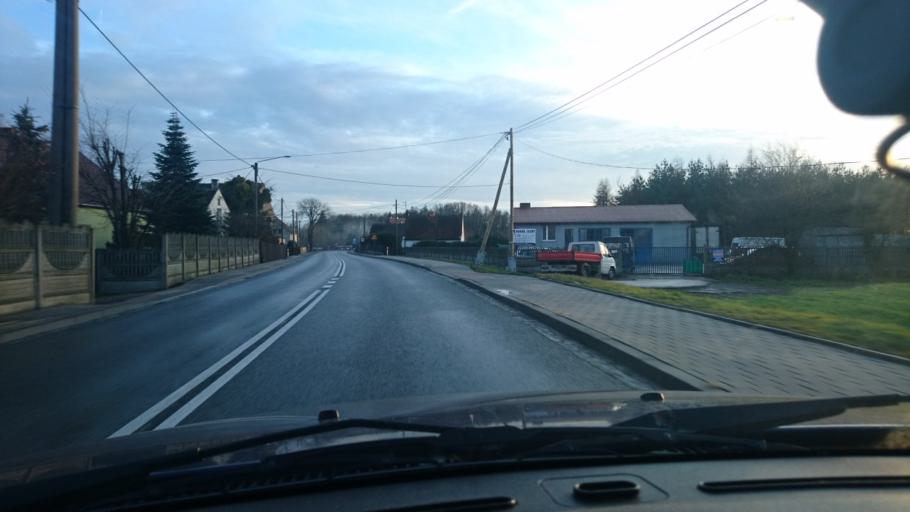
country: PL
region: Greater Poland Voivodeship
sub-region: Powiat kepinski
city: Opatow
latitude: 51.1674
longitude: 18.1468
